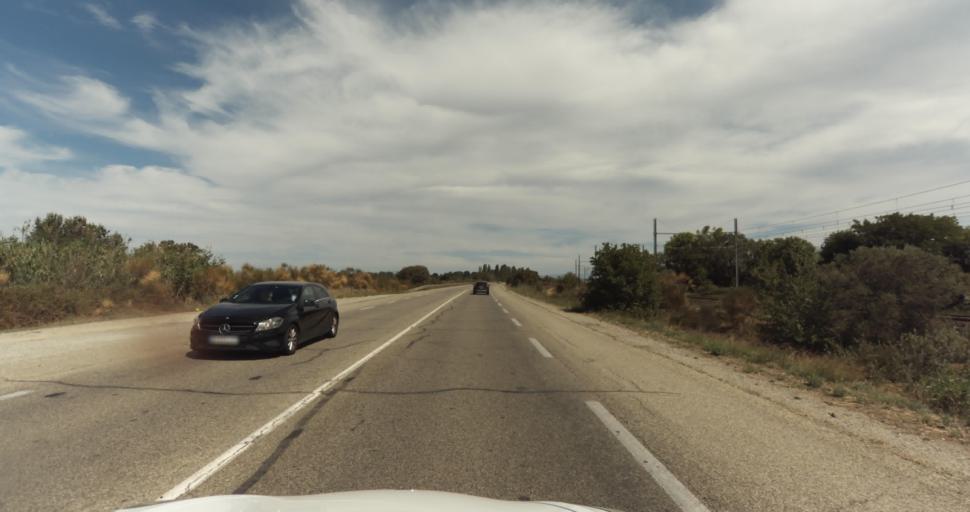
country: FR
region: Provence-Alpes-Cote d'Azur
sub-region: Departement des Bouches-du-Rhone
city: Istres
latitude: 43.5484
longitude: 4.9564
